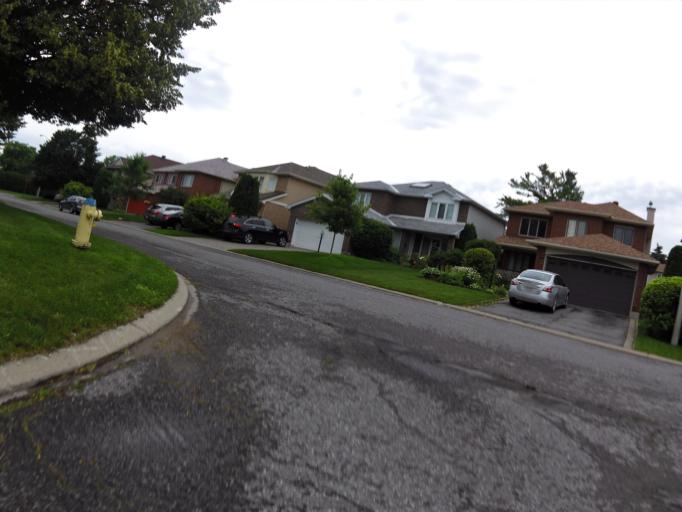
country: CA
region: Ontario
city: Bells Corners
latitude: 45.3370
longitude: -75.7664
